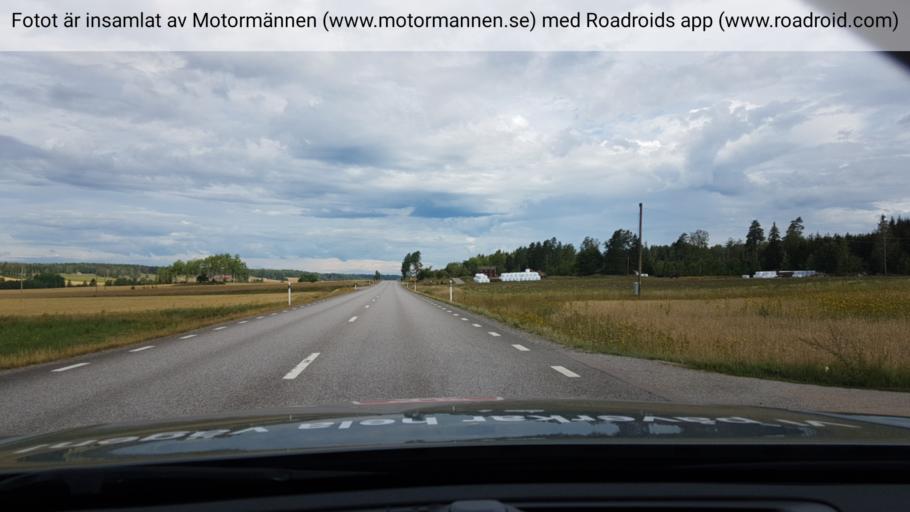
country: SE
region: Uppsala
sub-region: Heby Kommun
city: Morgongava
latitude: 59.8841
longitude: 16.9154
